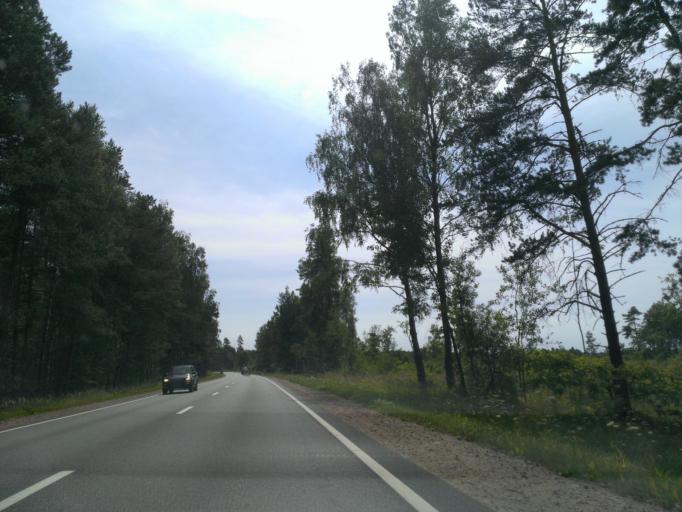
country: LV
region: Riga
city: Bergi
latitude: 56.9540
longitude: 24.3774
